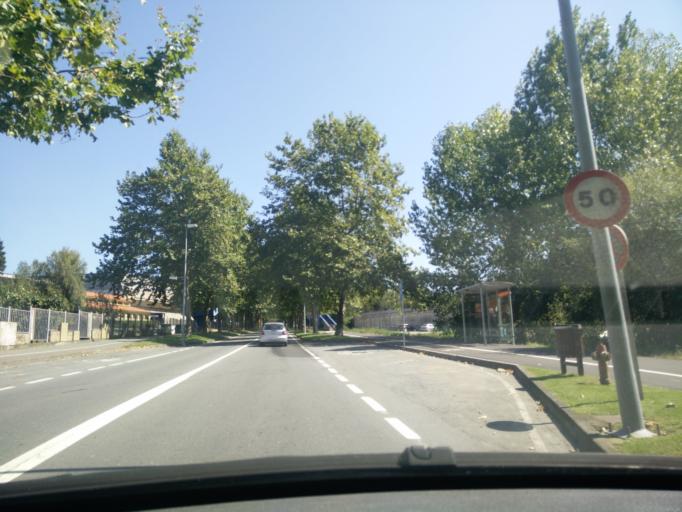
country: ES
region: Galicia
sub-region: Provincia da Coruna
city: Oleiros
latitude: 43.3395
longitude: -8.3582
